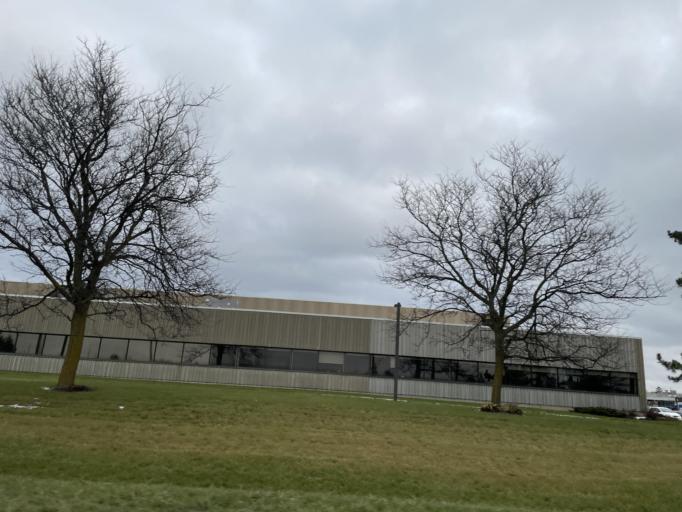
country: CA
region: Ontario
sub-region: Wellington County
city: Guelph
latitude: 43.5375
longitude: -80.3129
